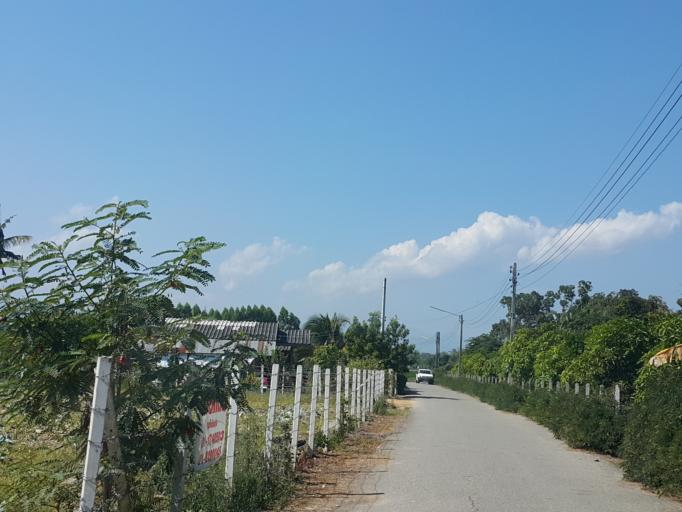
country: TH
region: Chiang Mai
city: Mae Taeng
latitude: 18.9986
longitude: 98.9833
